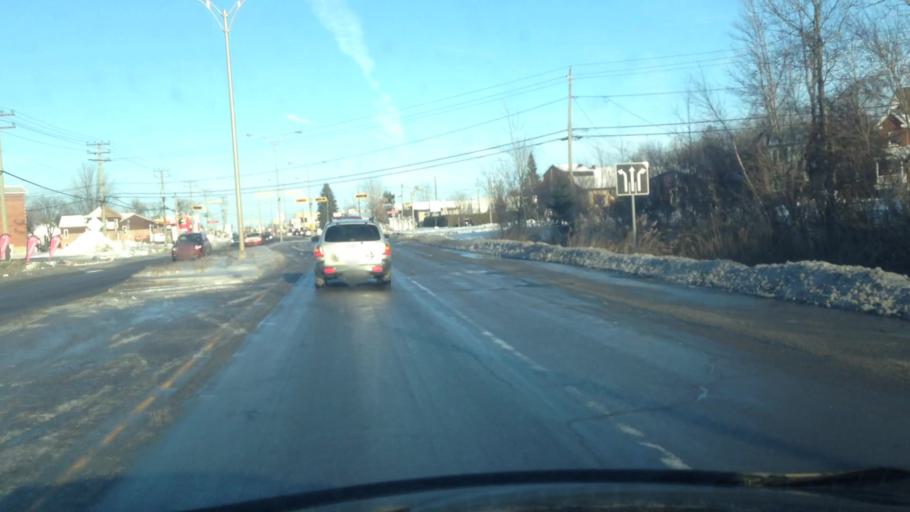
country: CA
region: Quebec
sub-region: Laurentides
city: Saint-Jerome
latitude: 45.7656
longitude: -73.9797
